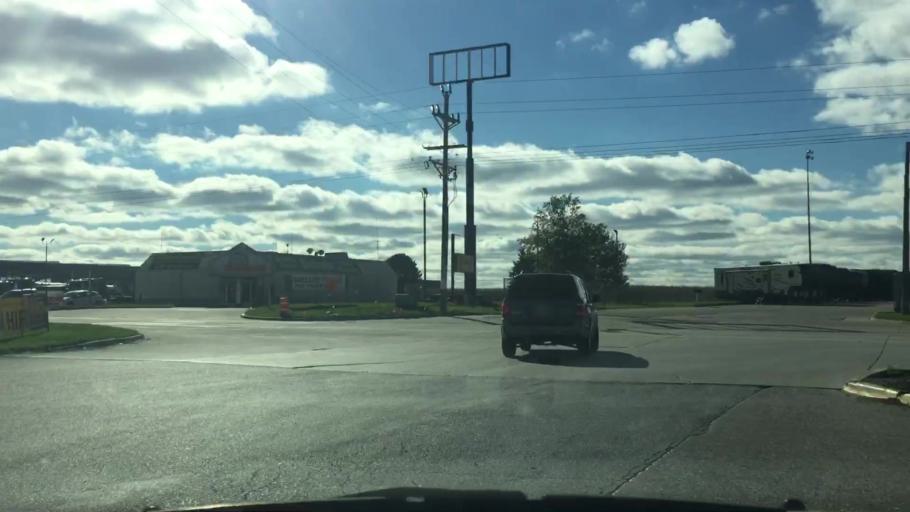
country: US
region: Iowa
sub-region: Scott County
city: Walcott
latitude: 41.6140
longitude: -90.7828
